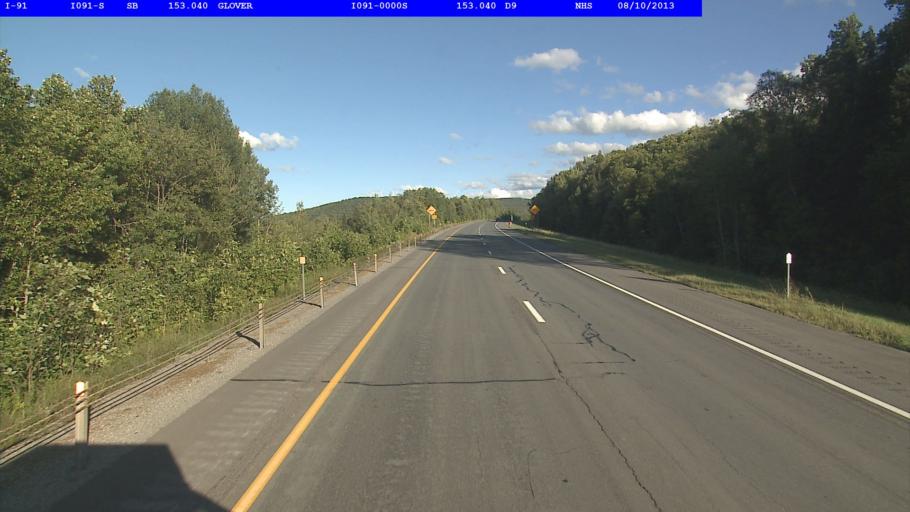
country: US
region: Vermont
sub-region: Caledonia County
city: Lyndonville
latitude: 44.7048
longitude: -72.1520
